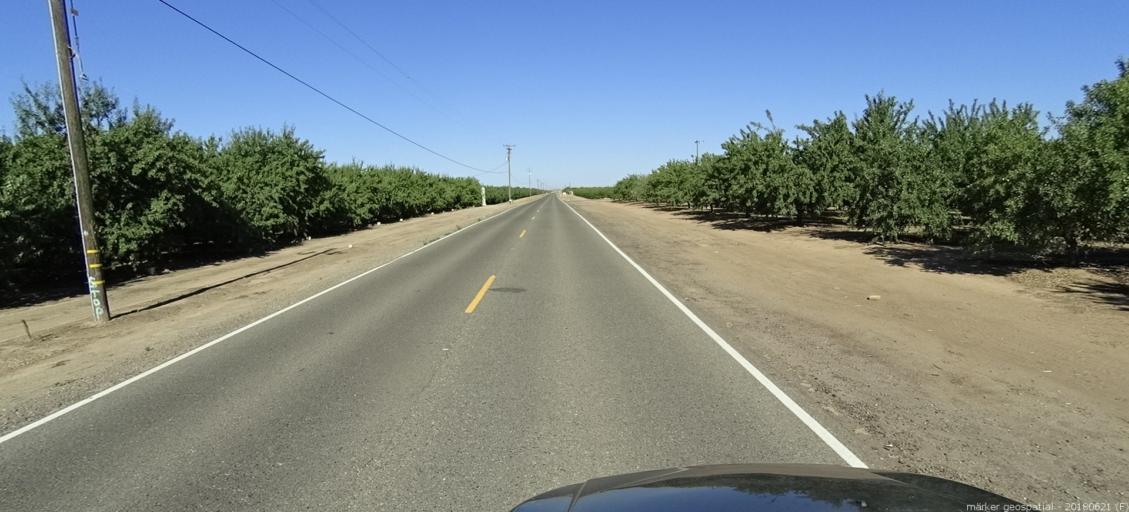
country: US
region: California
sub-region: Fresno County
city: Biola
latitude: 36.8514
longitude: -119.9233
